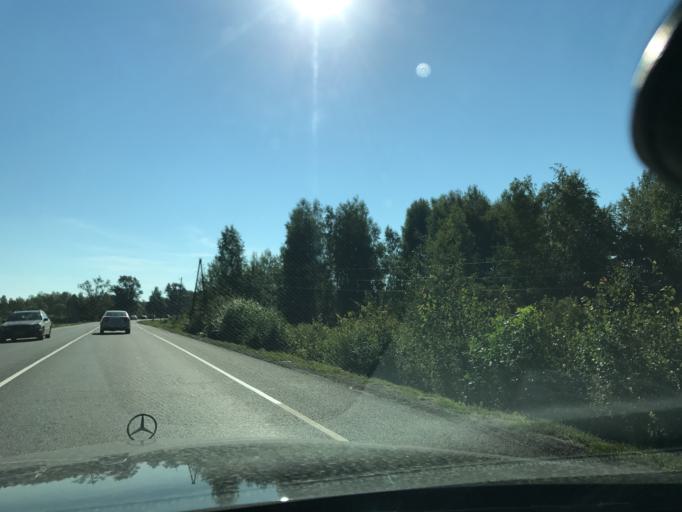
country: RU
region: Moskovskaya
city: Noginsk-9
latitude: 56.1035
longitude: 38.6439
